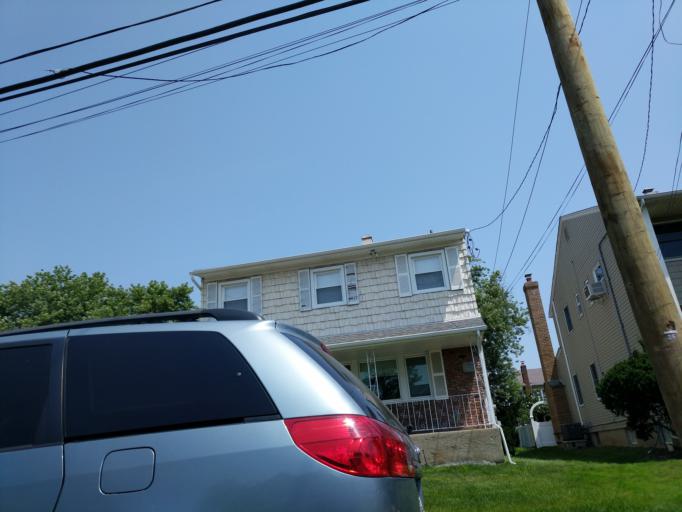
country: US
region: New York
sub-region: Nassau County
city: Cedarhurst
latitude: 40.6323
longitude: -73.7292
